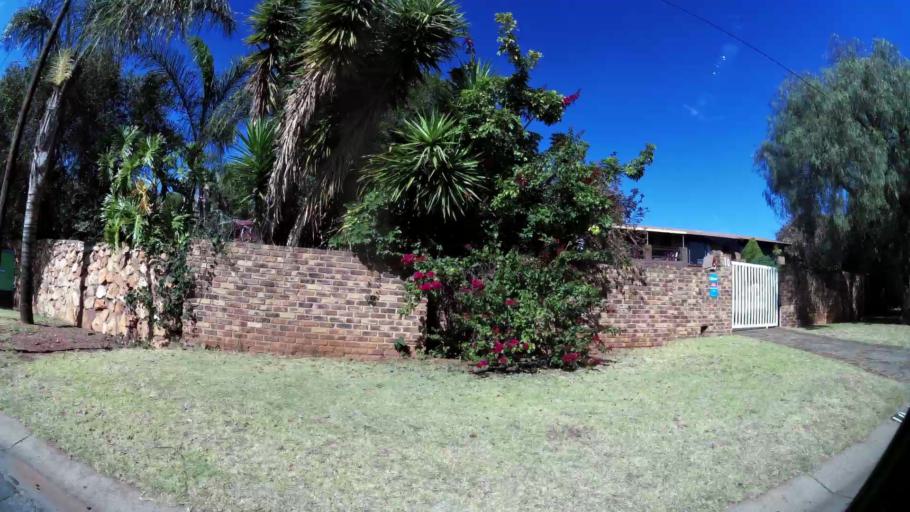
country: ZA
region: Gauteng
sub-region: City of Johannesburg Metropolitan Municipality
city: Roodepoort
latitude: -26.1162
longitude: 27.8549
